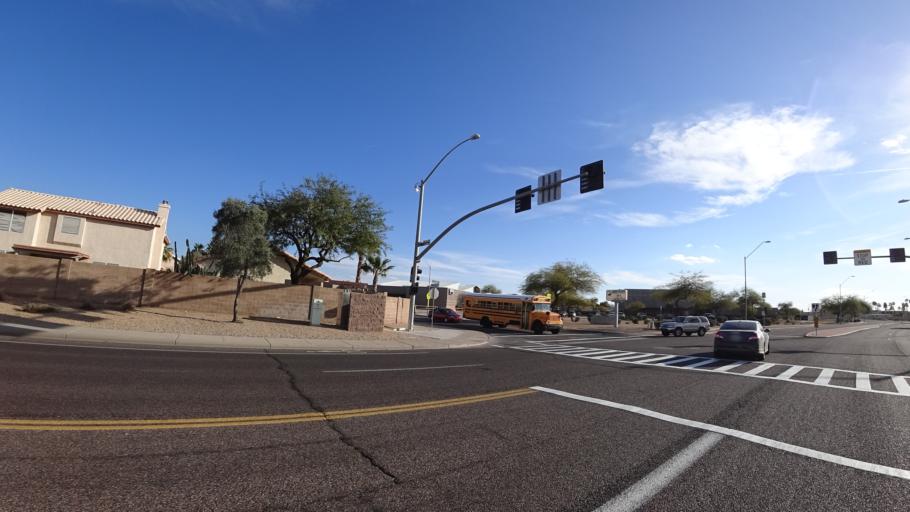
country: US
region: Arizona
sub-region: Maricopa County
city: Sun City
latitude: 33.6270
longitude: -112.2526
